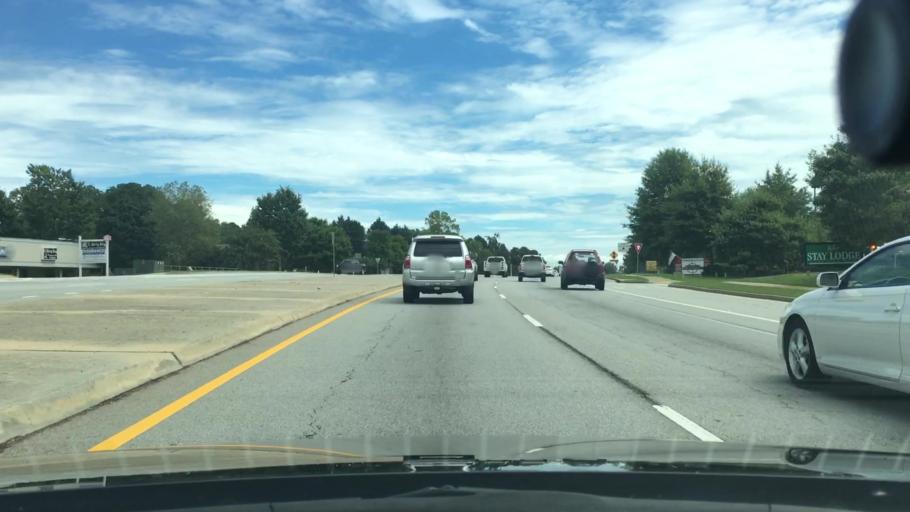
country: US
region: Georgia
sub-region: Coweta County
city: Newnan
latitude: 33.3999
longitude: -84.7680
